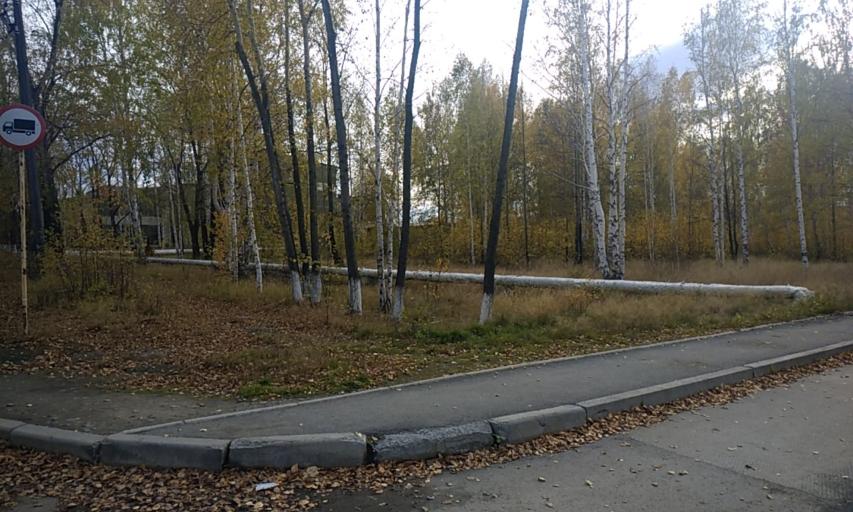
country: RU
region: Sverdlovsk
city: Krasnoural'sk
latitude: 58.3555
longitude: 60.0556
